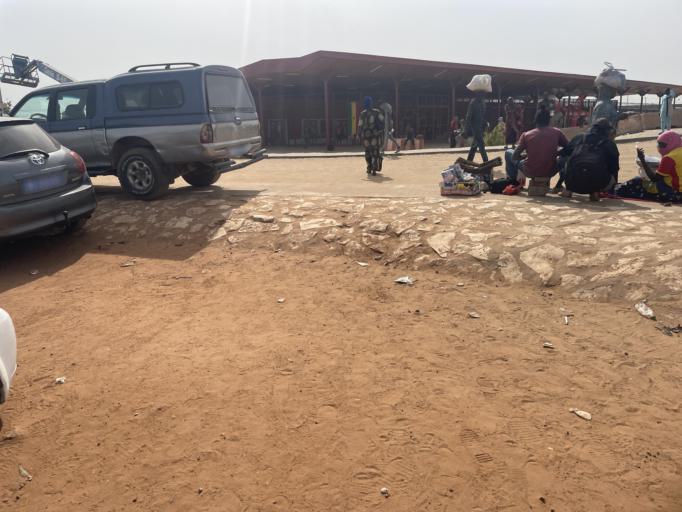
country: SN
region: Dakar
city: Pikine
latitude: 14.7601
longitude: -17.3802
